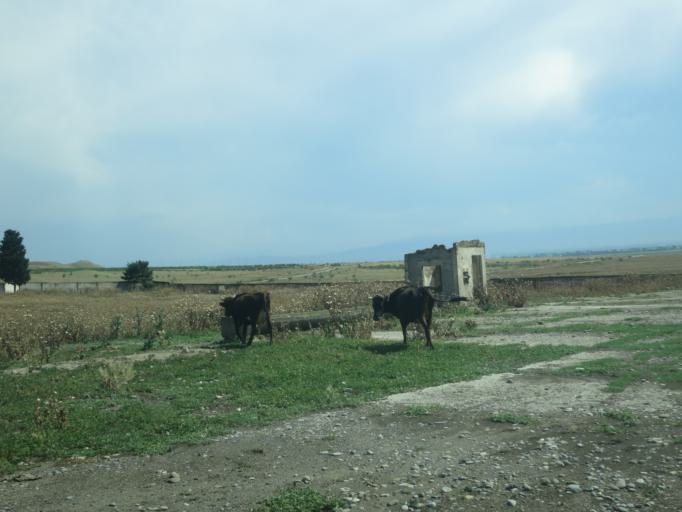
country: GE
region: Kvemo Kartli
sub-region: Gardabani
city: Gardabani
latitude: 41.4985
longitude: 45.1884
